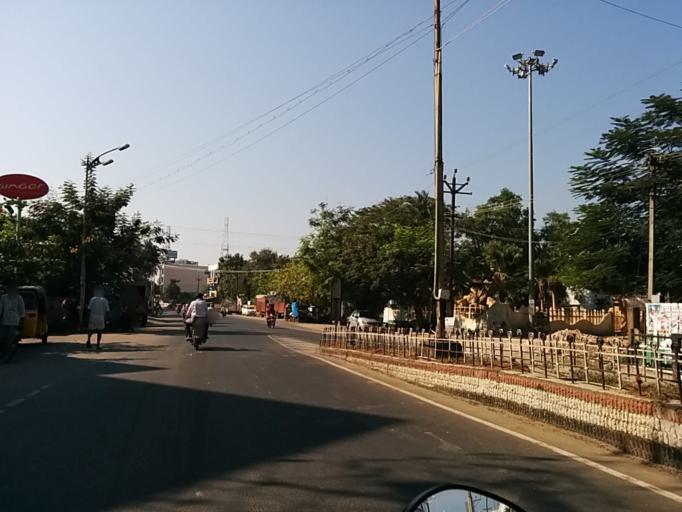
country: IN
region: Pondicherry
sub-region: Puducherry
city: Puducherry
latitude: 11.9525
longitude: 79.8297
